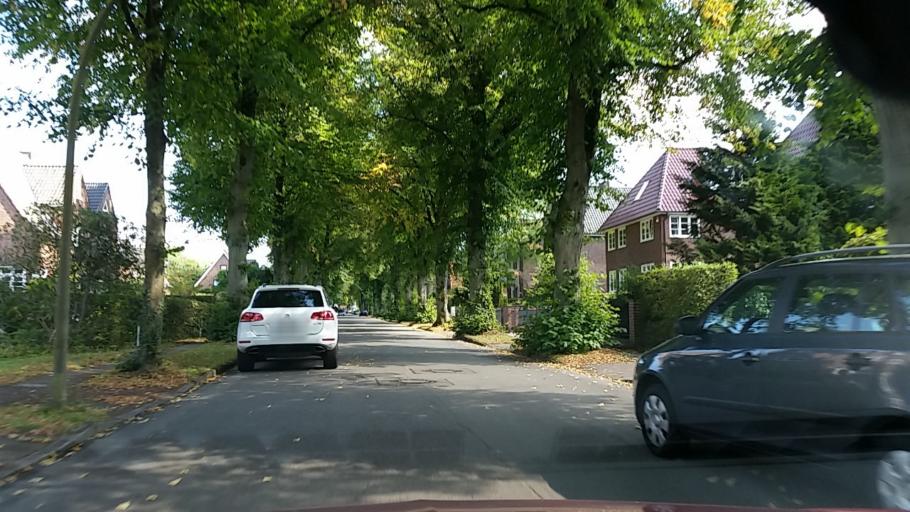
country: DE
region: Hamburg
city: Bergstedt
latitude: 53.6585
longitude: 10.1527
